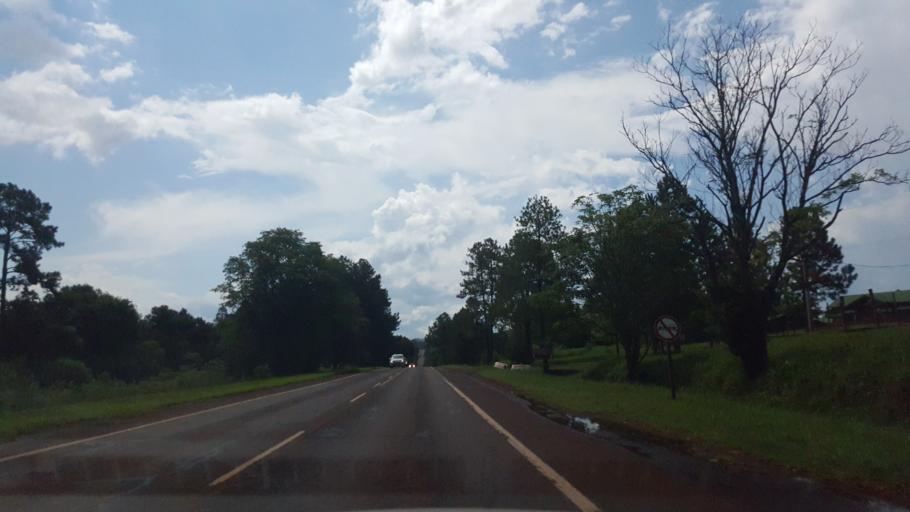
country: AR
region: Misiones
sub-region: Departamento de Eldorado
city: Eldorado
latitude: -26.3080
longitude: -54.6163
